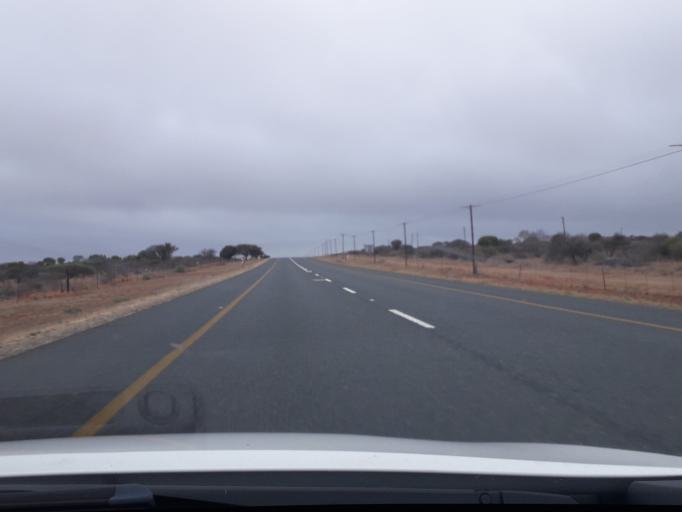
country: ZA
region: Limpopo
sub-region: Vhembe District Municipality
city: Louis Trichardt
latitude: -23.4197
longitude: 29.7521
